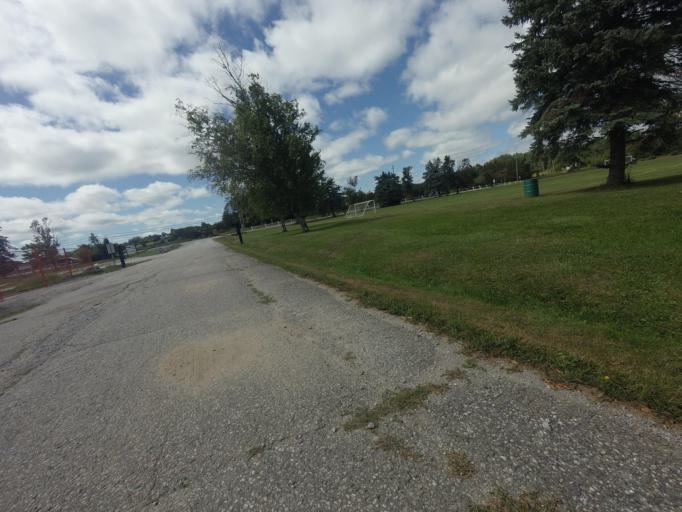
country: CA
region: Ontario
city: Uxbridge
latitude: 44.1253
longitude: -79.1265
